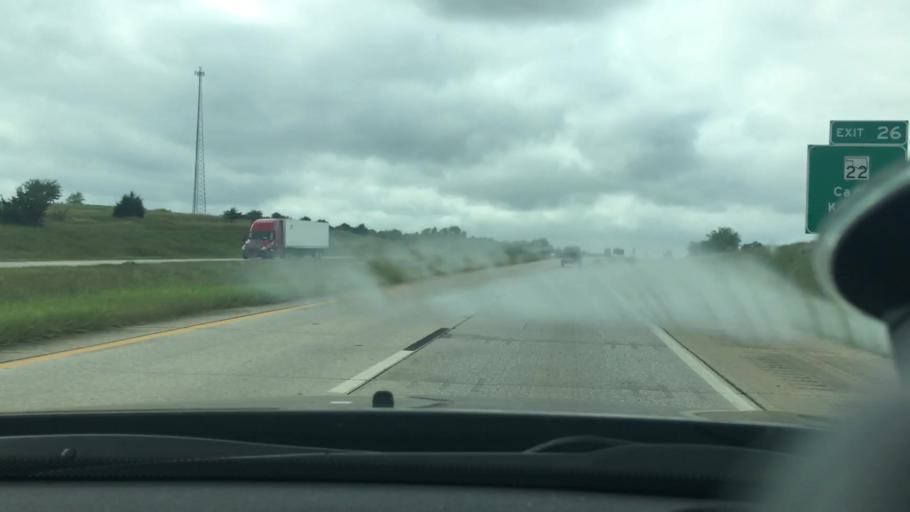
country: US
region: Oklahoma
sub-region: Bryan County
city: Durant
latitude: 34.1432
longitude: -96.2666
